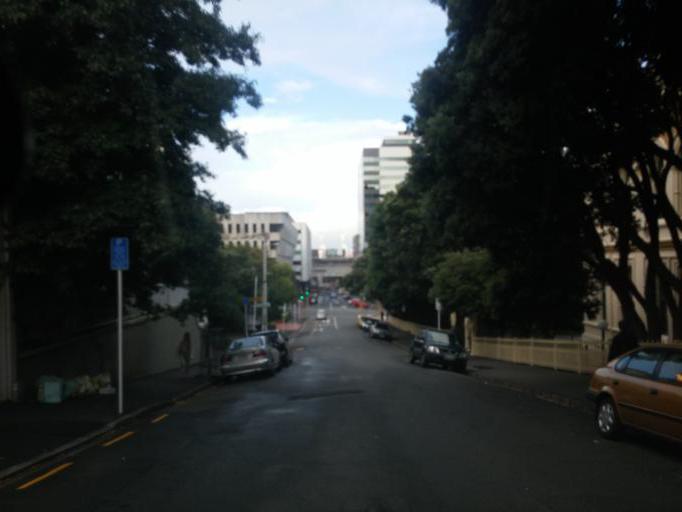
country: NZ
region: Wellington
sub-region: Wellington City
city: Wellington
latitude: -41.2768
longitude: 174.7762
